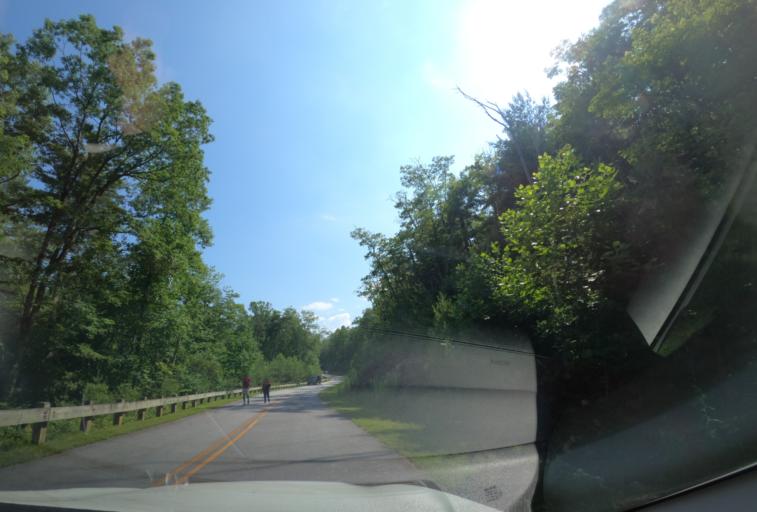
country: US
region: North Carolina
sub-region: Transylvania County
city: Brevard
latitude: 35.0915
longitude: -82.9496
